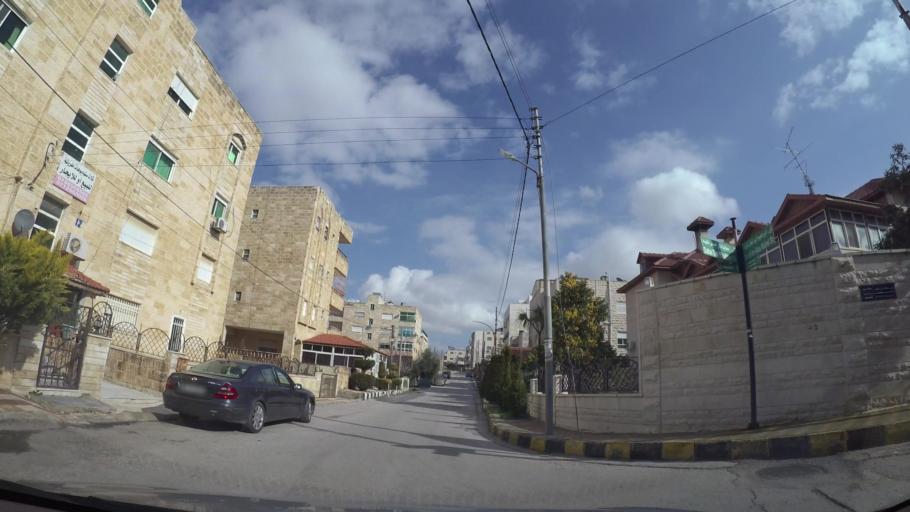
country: JO
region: Amman
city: Al Jubayhah
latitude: 32.0181
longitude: 35.8606
